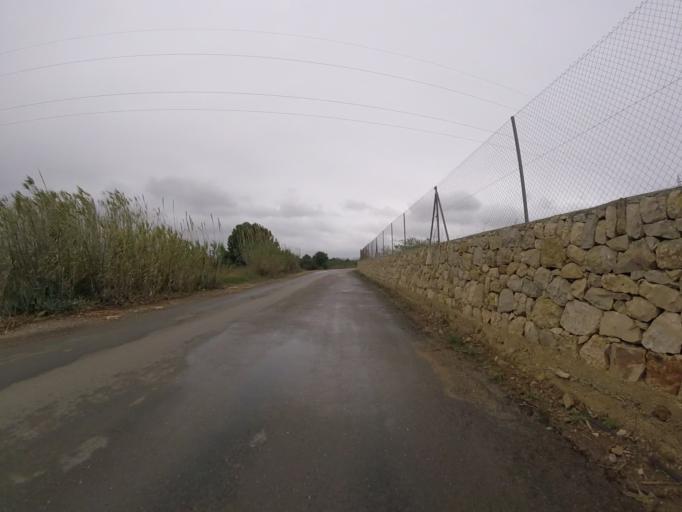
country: ES
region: Valencia
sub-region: Provincia de Castello
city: Alcoceber
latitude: 40.2398
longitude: 0.2495
